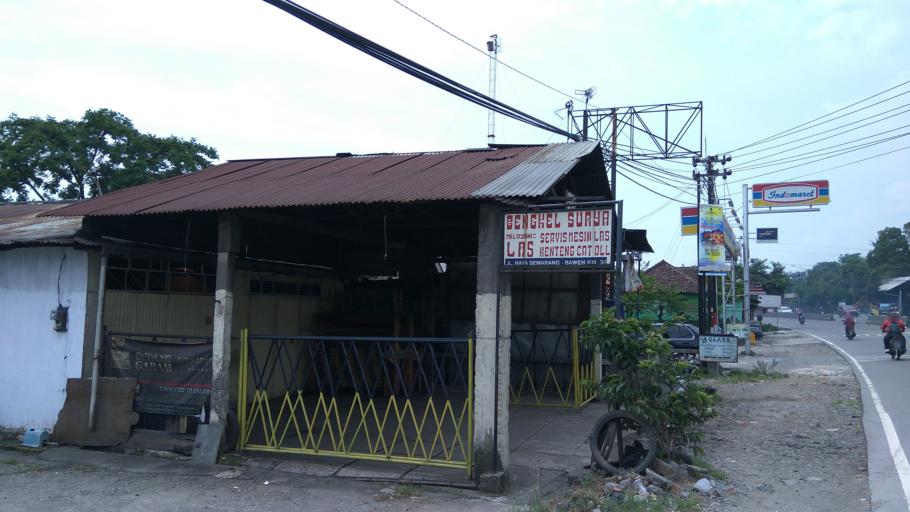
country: ID
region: Central Java
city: Ambarawa
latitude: -7.2118
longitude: 110.4247
